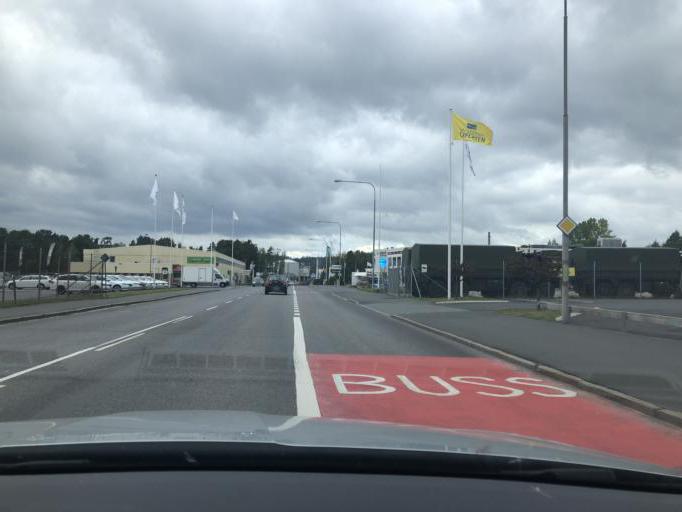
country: SE
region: Joenkoeping
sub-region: Jonkopings Kommun
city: Jonkoping
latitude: 57.7668
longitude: 14.1752
